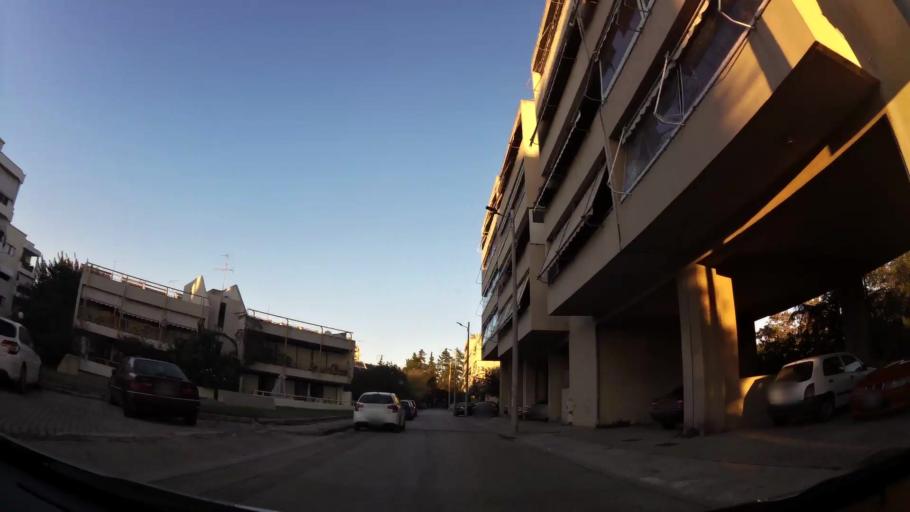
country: GR
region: Attica
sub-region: Nomarchia Athinas
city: Lykovrysi
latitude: 38.0678
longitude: 23.7906
